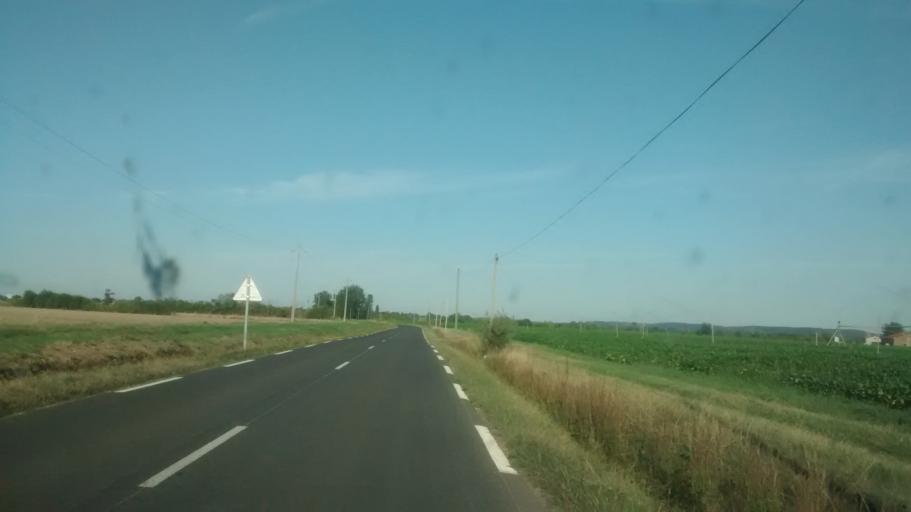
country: FR
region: Midi-Pyrenees
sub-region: Departement de la Haute-Garonne
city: Lherm
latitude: 43.4340
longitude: 1.2391
